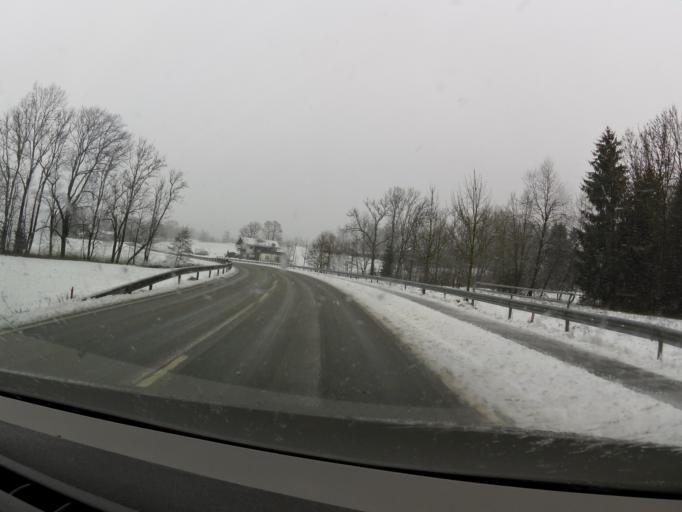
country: DE
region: Bavaria
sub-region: Upper Bavaria
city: Gmund am Tegernsee
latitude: 47.7574
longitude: 11.7057
